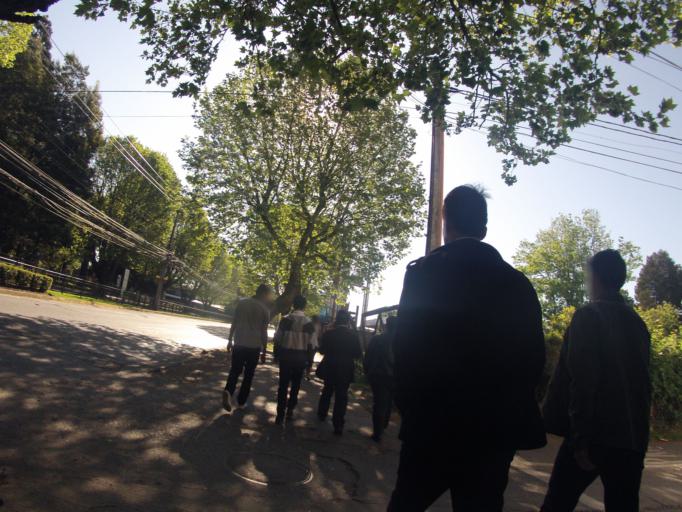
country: CL
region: Araucania
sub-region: Provincia de Cautin
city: Temuco
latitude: -38.7367
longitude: -72.6022
